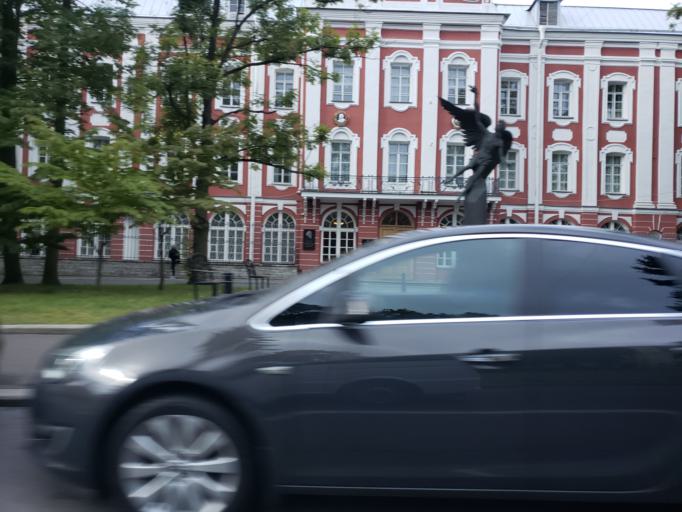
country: RU
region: St.-Petersburg
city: Saint Petersburg
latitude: 59.9417
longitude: 30.2999
